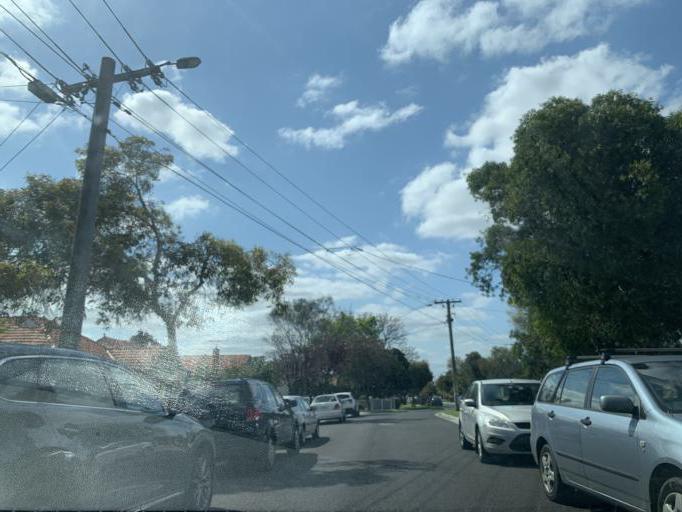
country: AU
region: Victoria
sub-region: Moreland
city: Coburg
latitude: -37.7456
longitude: 144.9745
